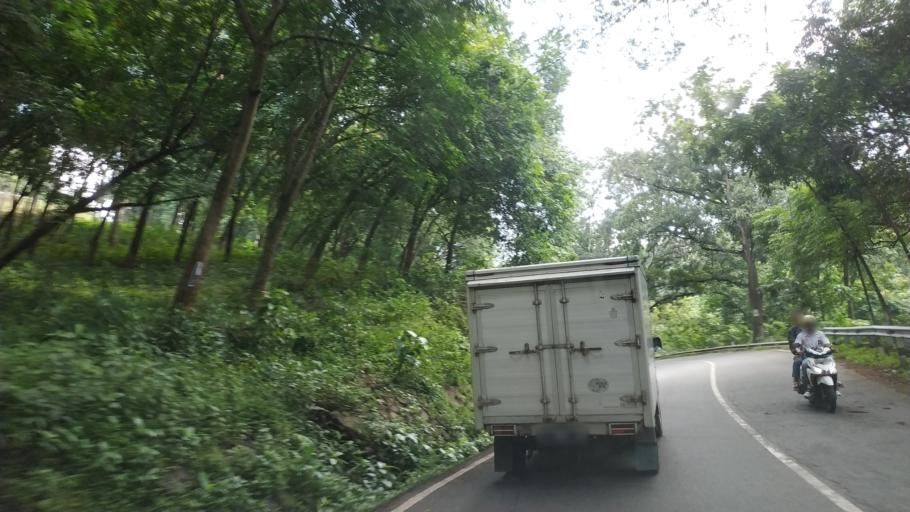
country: ID
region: Central Java
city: Weleri
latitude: -7.0015
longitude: 110.0647
